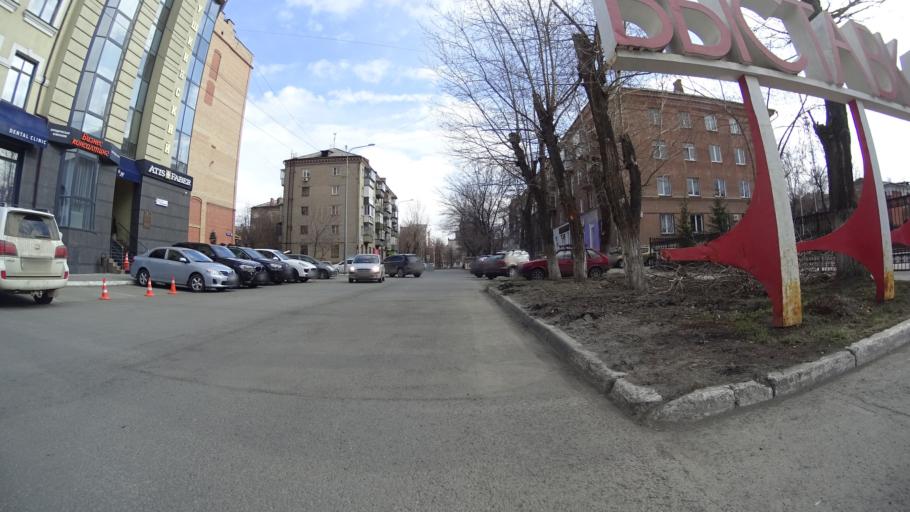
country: RU
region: Chelyabinsk
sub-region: Gorod Chelyabinsk
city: Chelyabinsk
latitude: 55.1565
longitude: 61.4103
